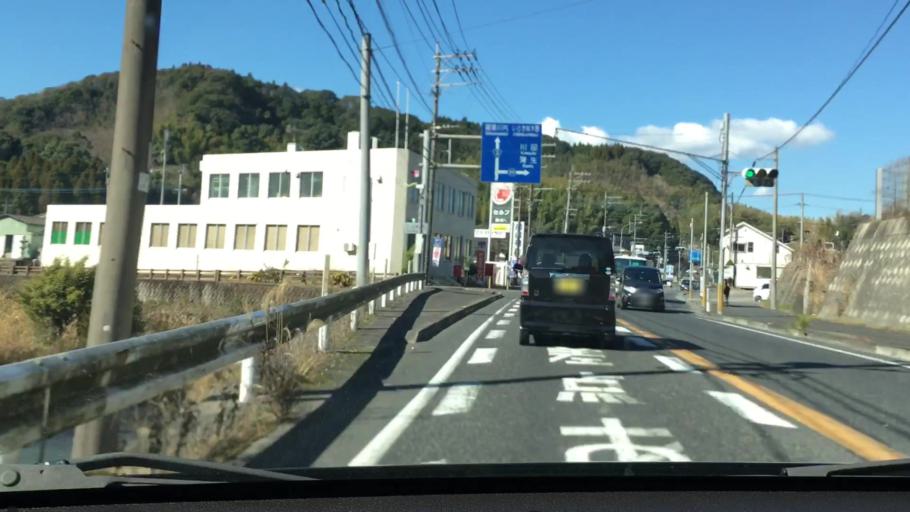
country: JP
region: Kagoshima
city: Ijuin
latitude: 31.6539
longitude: 130.4980
